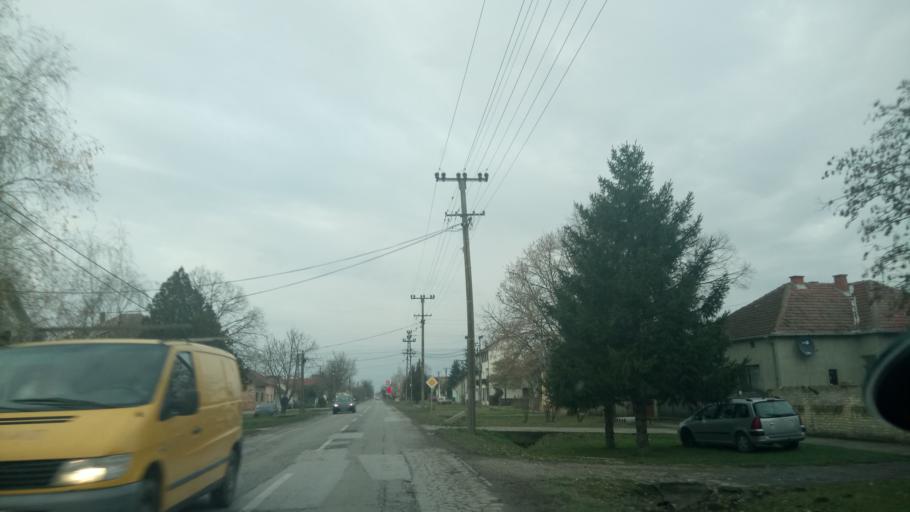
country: RS
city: Vojka
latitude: 44.9460
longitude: 20.1542
